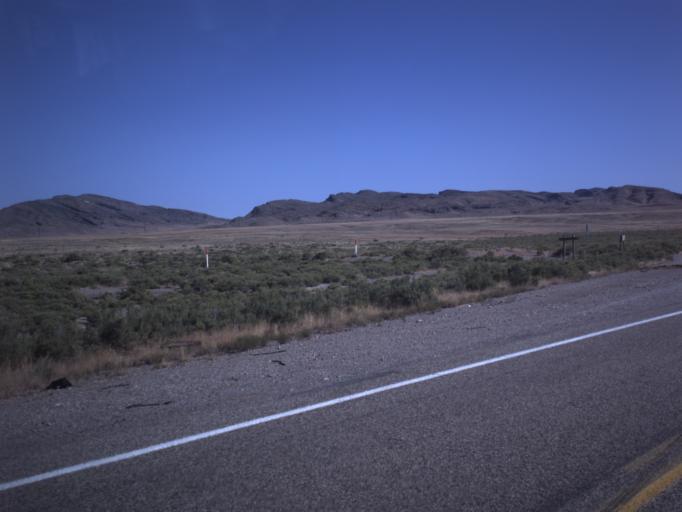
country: US
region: Utah
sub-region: Beaver County
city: Milford
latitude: 38.7329
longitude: -112.9657
